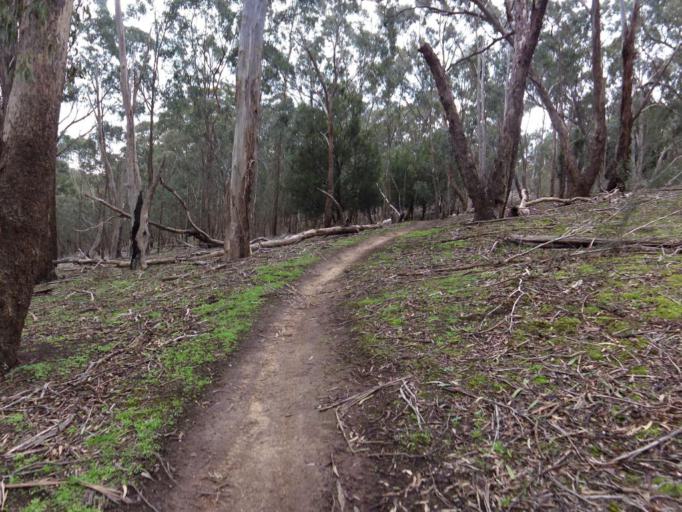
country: AU
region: Victoria
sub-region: Banyule
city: Watsonia North
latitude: -37.6788
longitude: 145.0945
